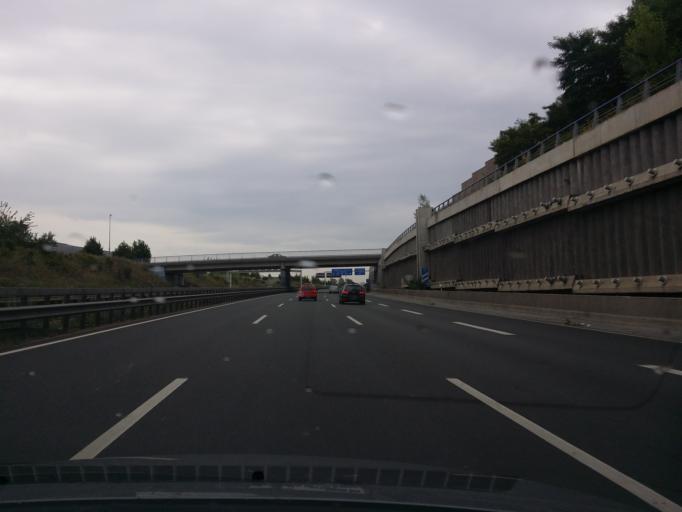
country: DE
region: Rheinland-Pfalz
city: Mainz
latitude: 49.9748
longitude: 8.2797
